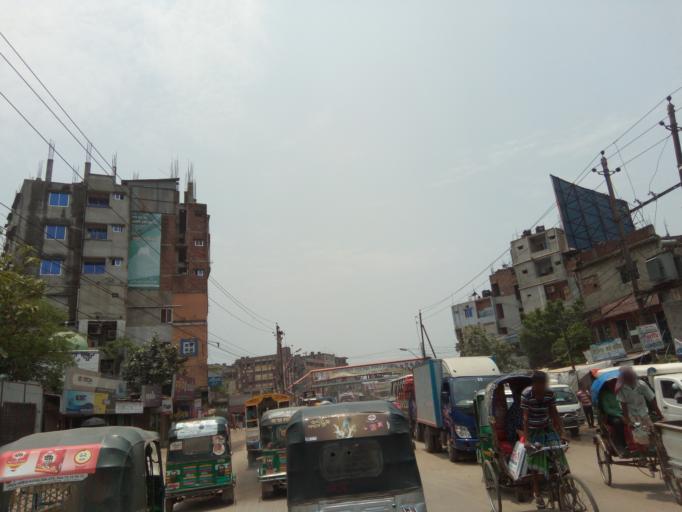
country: BD
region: Dhaka
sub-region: Dhaka
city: Dhaka
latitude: 23.6945
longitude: 90.4353
